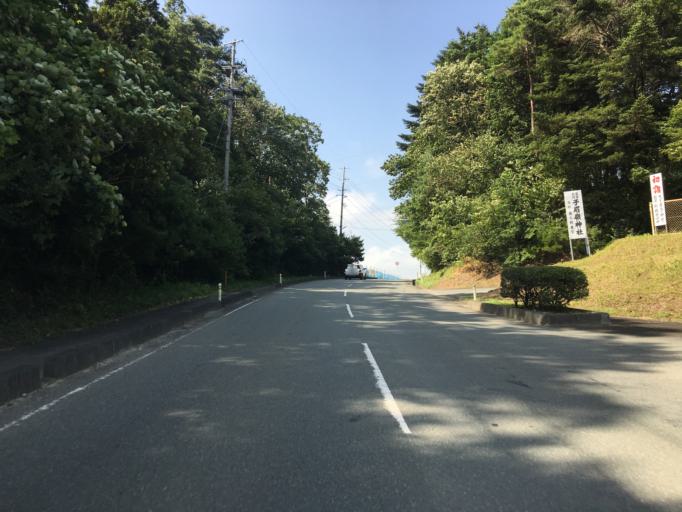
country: JP
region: Miyagi
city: Marumori
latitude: 37.8518
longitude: 140.8958
